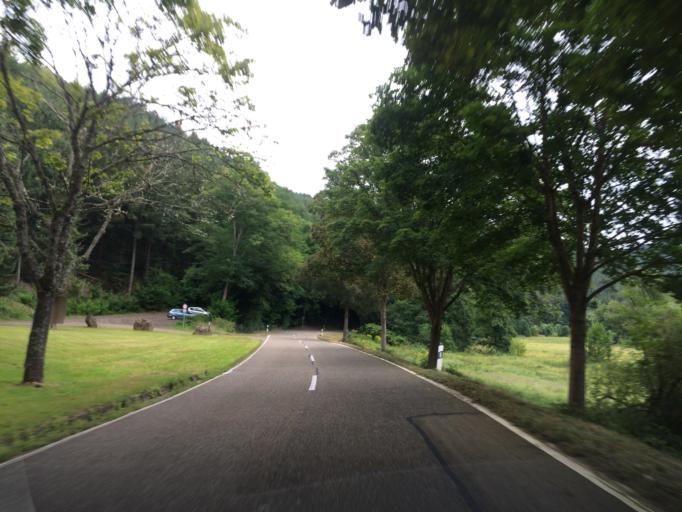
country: DE
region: Rheinland-Pfalz
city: Niederschlettenbach
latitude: 49.0835
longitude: 7.8510
